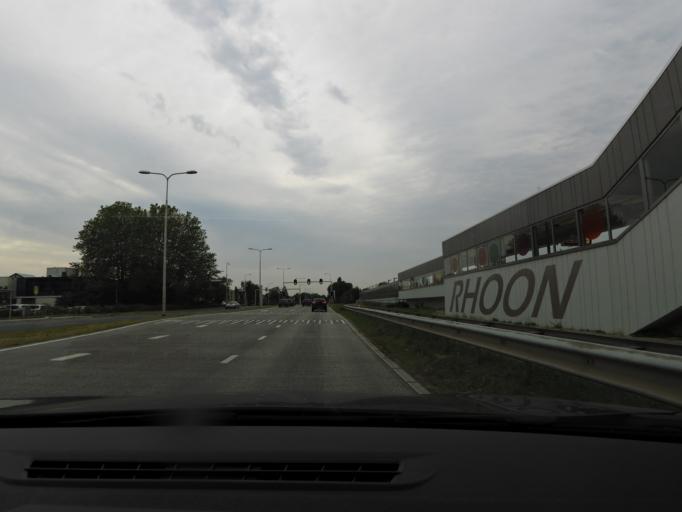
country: NL
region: South Holland
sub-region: Gemeente Albrandswaard
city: Rhoon
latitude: 51.8590
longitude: 4.4197
